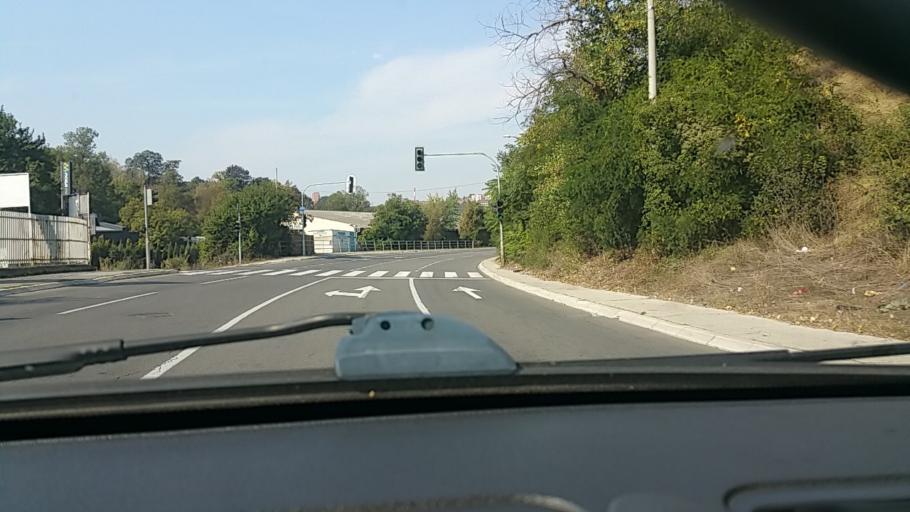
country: RS
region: Central Serbia
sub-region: Belgrade
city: Rakovica
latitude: 44.7360
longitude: 20.4451
